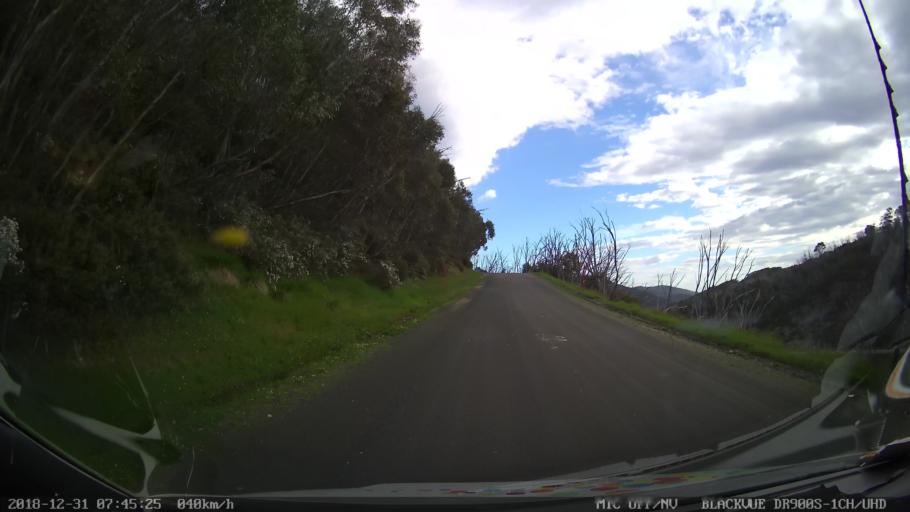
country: AU
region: New South Wales
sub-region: Snowy River
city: Jindabyne
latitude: -36.3644
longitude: 148.4032
